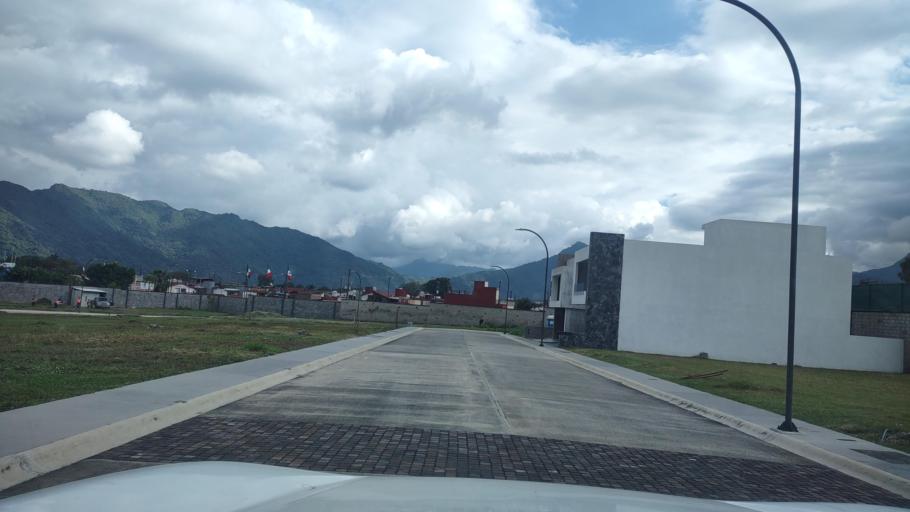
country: MX
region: Veracruz
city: Orizaba
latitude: 18.8423
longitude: -97.0886
